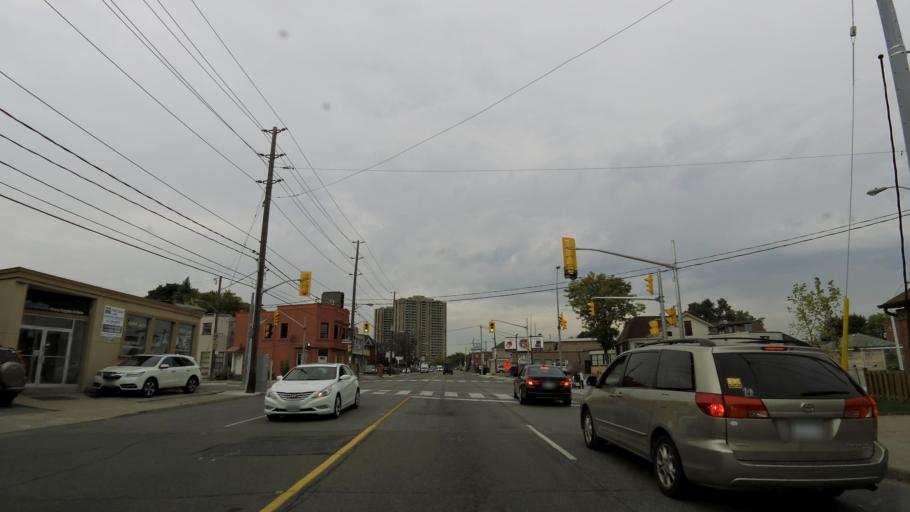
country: CA
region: Ontario
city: Etobicoke
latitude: 43.6963
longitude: -79.5077
